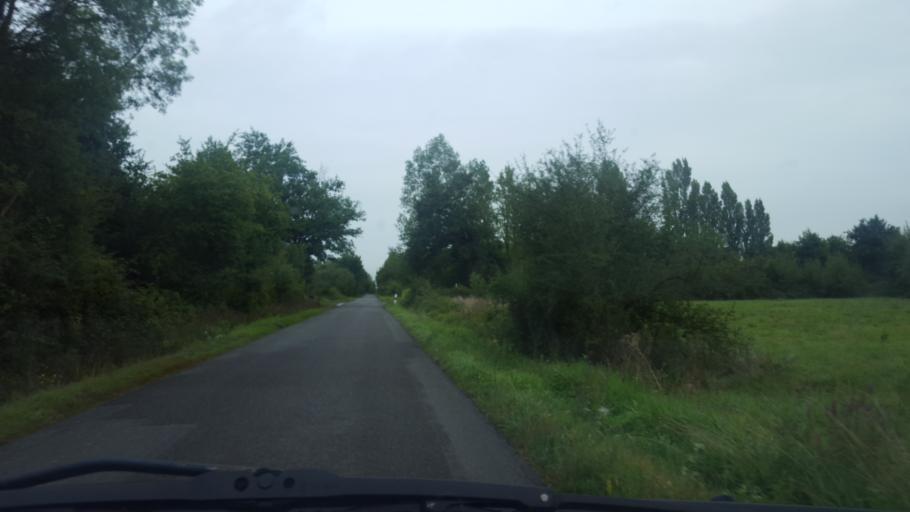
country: FR
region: Pays de la Loire
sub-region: Departement de la Loire-Atlantique
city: Saint-Philbert-de-Grand-Lieu
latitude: 47.0419
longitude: -1.6655
